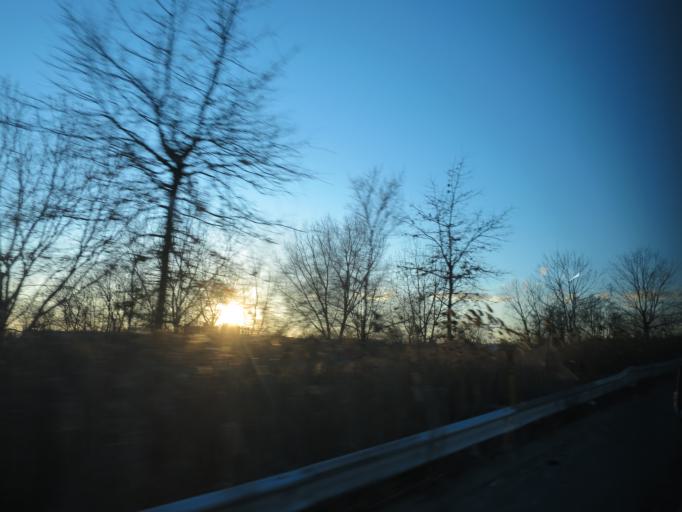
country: US
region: New York
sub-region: Queens County
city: Jamaica
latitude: 40.6653
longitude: -73.7915
